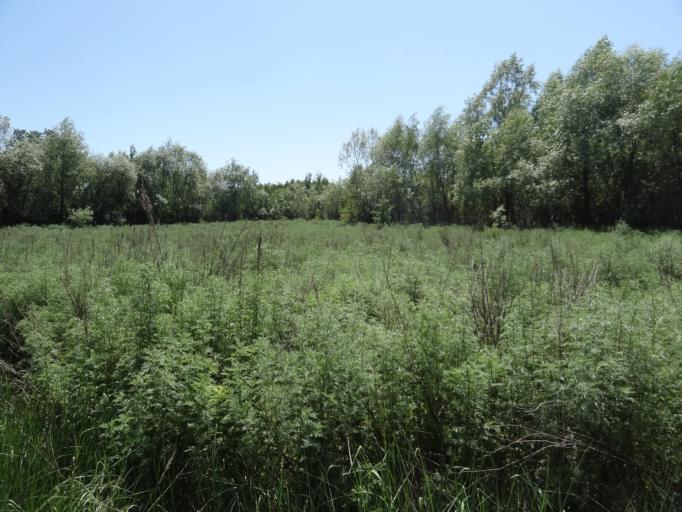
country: RU
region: Saratov
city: Krasnyy Oktyabr'
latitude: 51.3099
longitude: 45.5500
